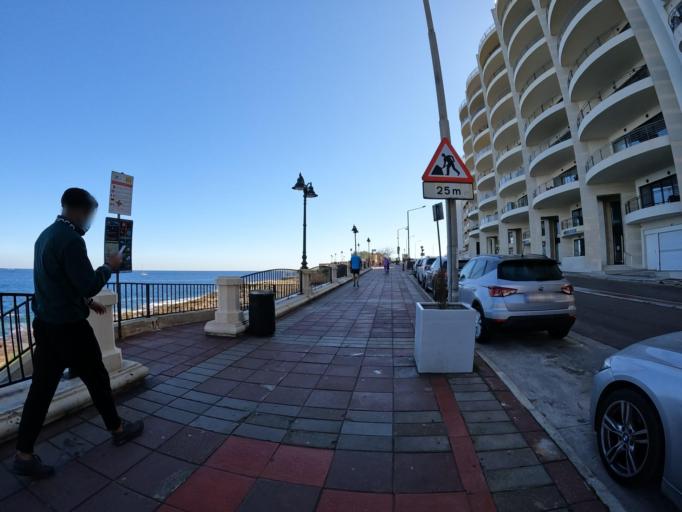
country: MT
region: Tas-Sliema
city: Sliema
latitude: 35.9112
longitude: 14.5081
